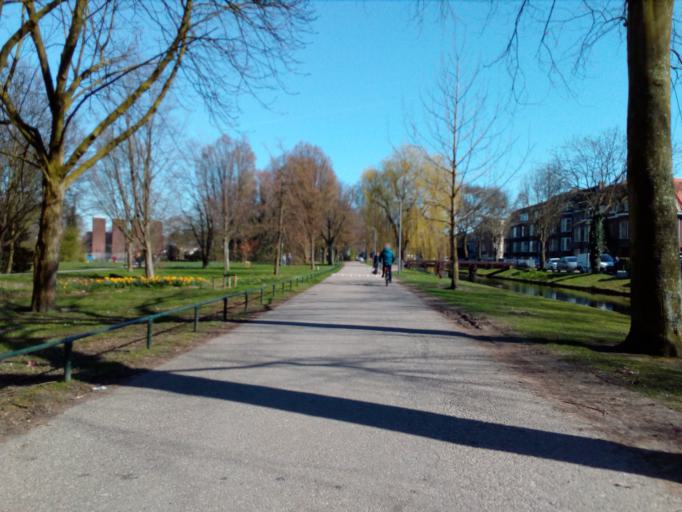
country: NL
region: South Holland
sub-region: Gemeente Rotterdam
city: Rotterdam
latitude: 51.9465
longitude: 4.4691
